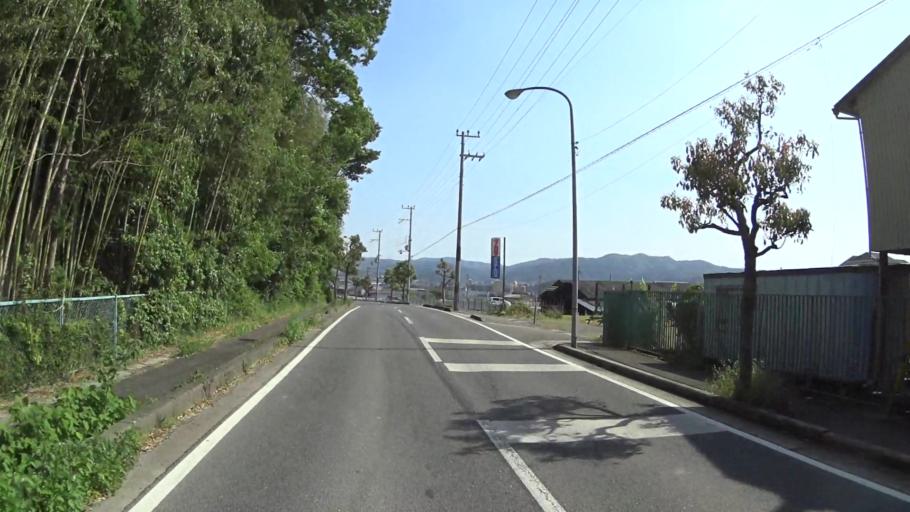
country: JP
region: Kyoto
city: Kameoka
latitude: 35.0268
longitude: 135.5873
